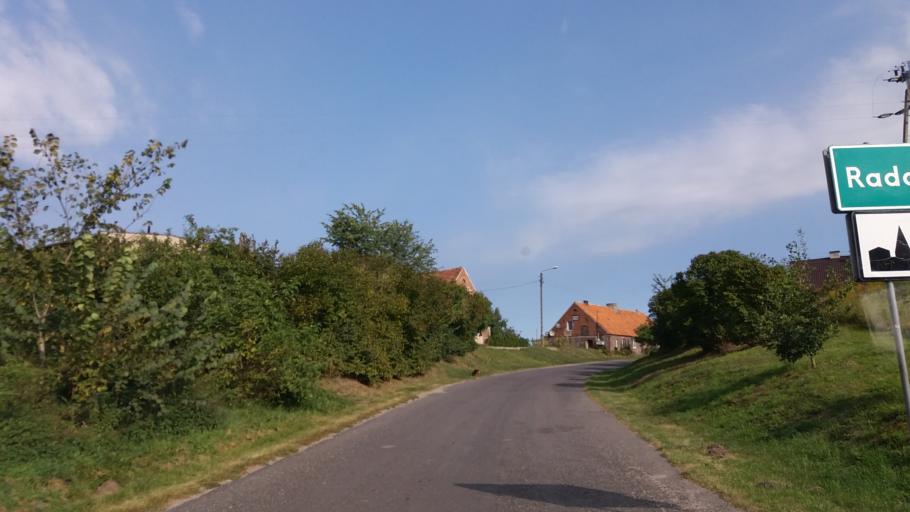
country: PL
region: West Pomeranian Voivodeship
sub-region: Powiat stargardzki
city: Suchan
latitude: 53.2262
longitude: 15.3418
